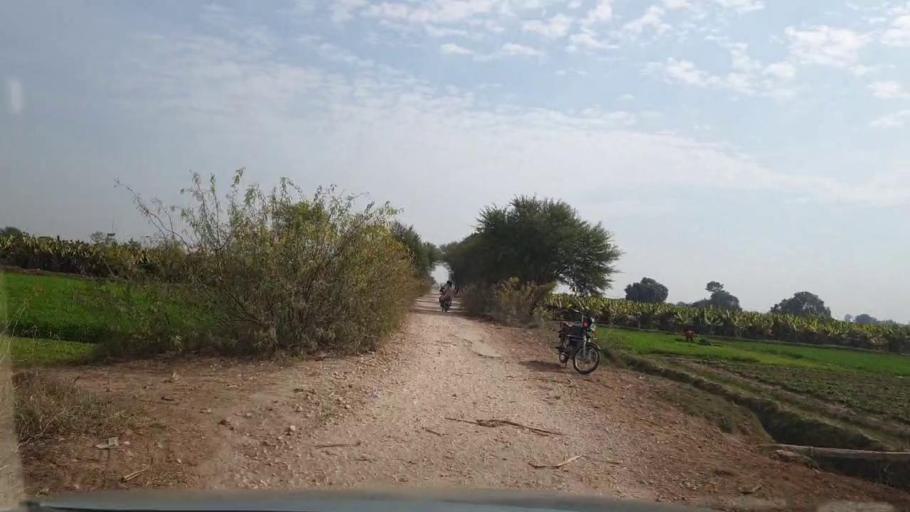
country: PK
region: Sindh
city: Tando Jam
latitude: 25.5240
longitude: 68.5594
